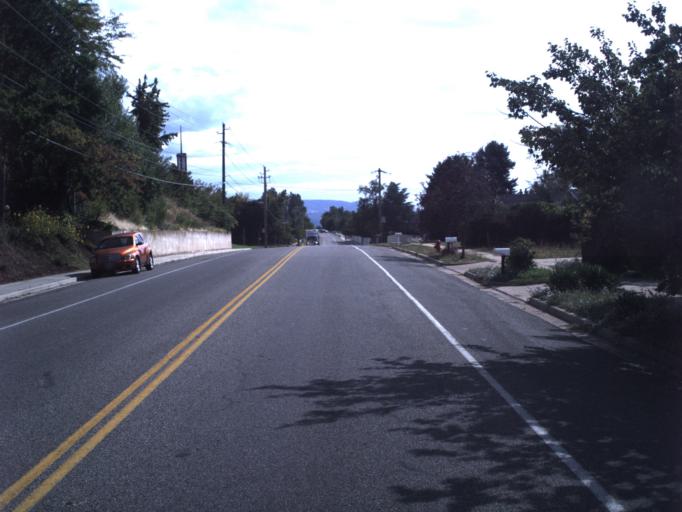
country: US
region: Utah
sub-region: Davis County
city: Farmington
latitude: 40.9702
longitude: -111.8834
